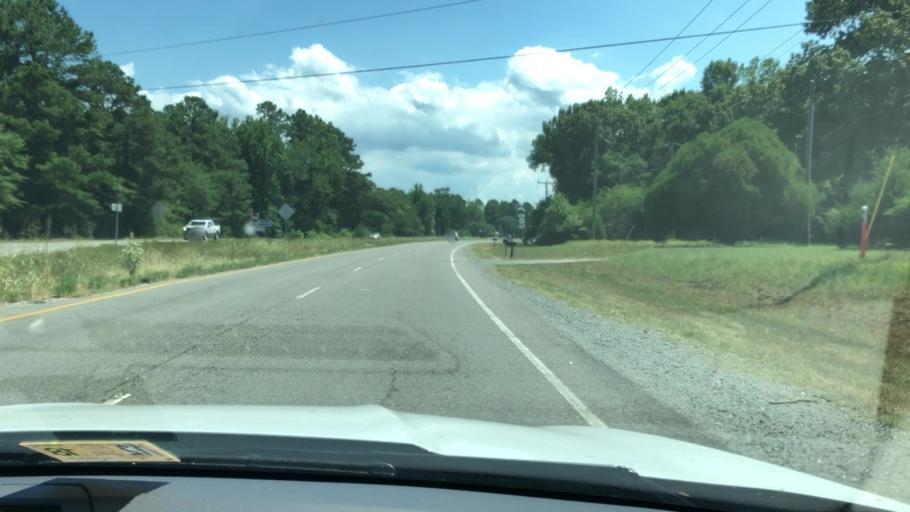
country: US
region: Virginia
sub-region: Middlesex County
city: Saluda
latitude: 37.5841
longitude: -76.6031
